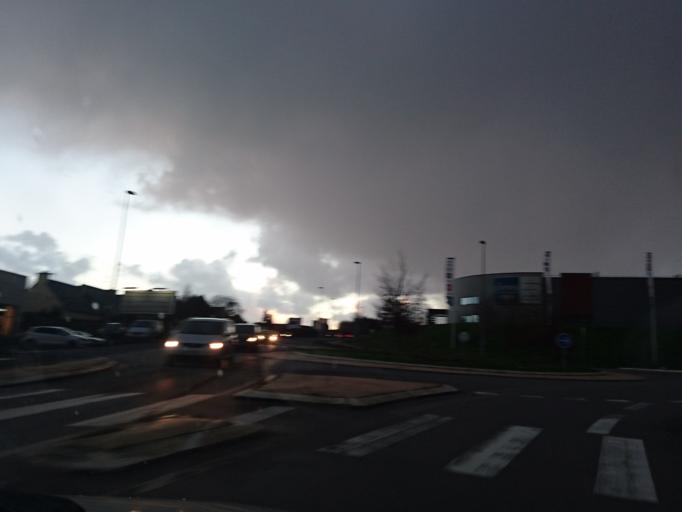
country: FR
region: Brittany
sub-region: Departement du Finistere
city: Le Relecq-Kerhuon
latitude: 48.4157
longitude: -4.4350
